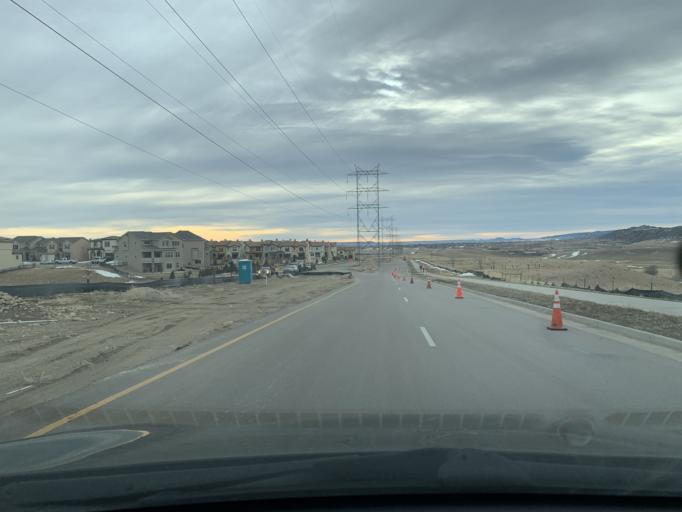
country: US
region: Colorado
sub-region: Jefferson County
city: West Pleasant View
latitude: 39.6722
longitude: -105.1817
